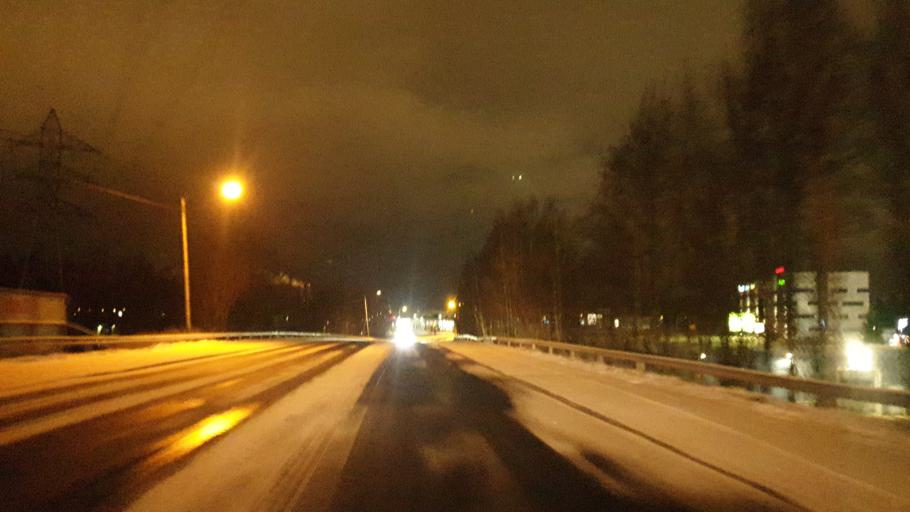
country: FI
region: Northern Ostrobothnia
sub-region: Oulu
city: Oulu
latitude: 64.9891
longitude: 25.4692
